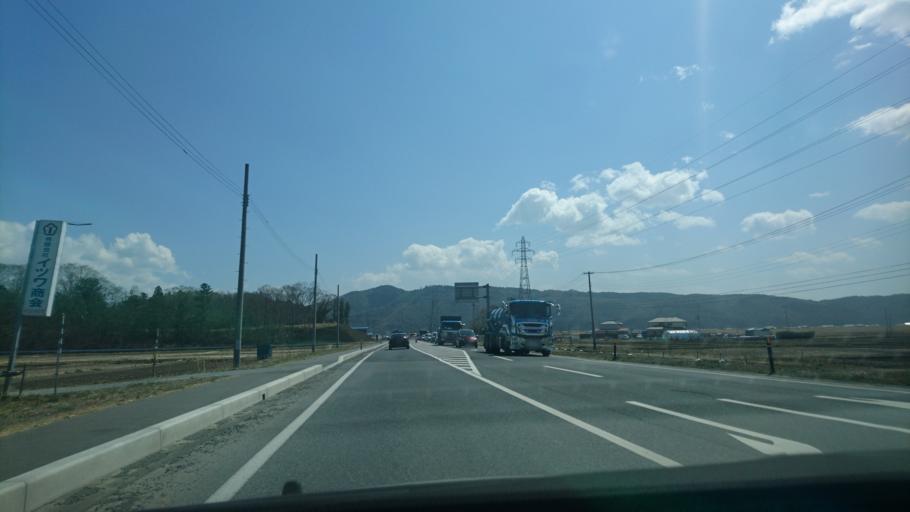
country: JP
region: Miyagi
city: Ishinomaki
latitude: 38.4524
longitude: 141.3131
